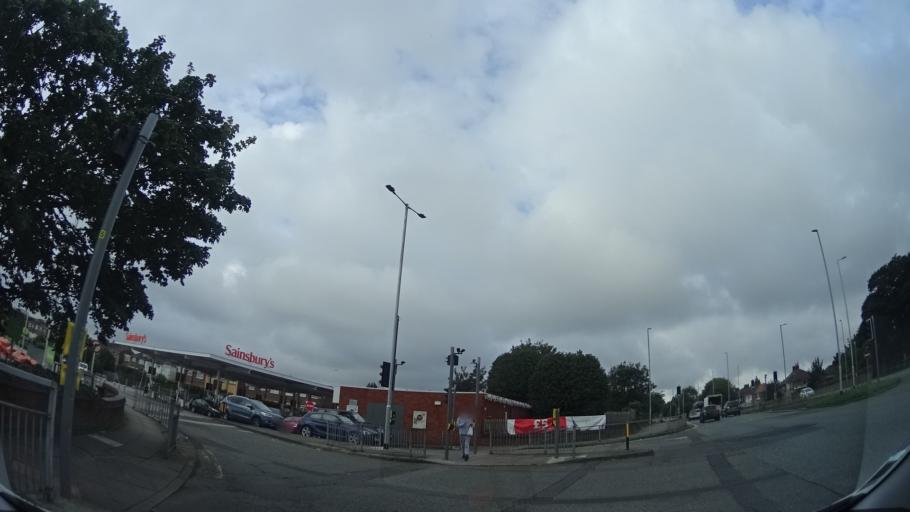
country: GB
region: England
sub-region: Knowsley
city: Knowsley
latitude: 53.4167
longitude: -2.8995
